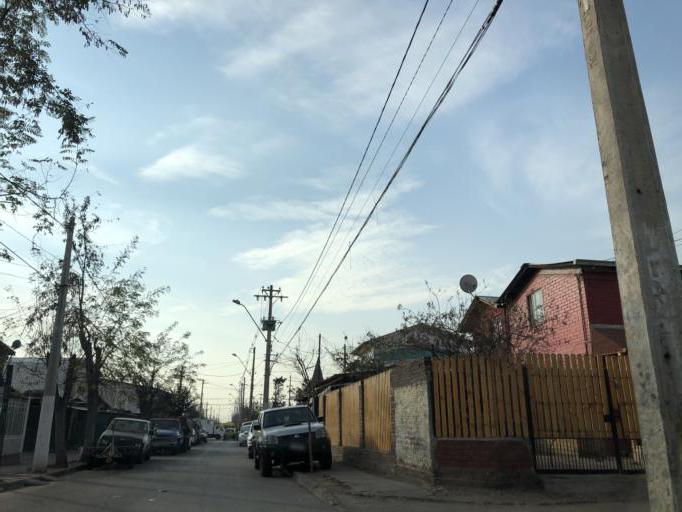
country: CL
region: Santiago Metropolitan
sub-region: Provincia de Cordillera
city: Puente Alto
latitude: -33.6048
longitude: -70.5597
